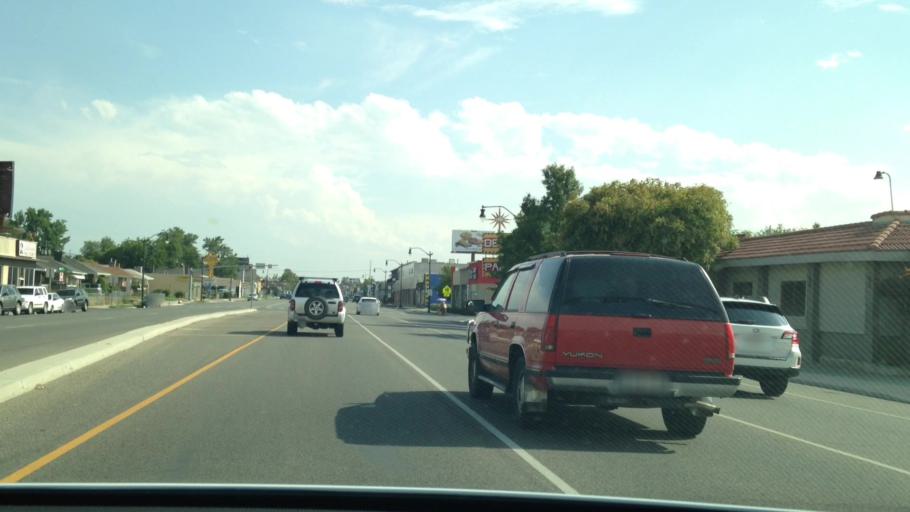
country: US
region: Utah
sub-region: Salt Lake County
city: Salt Lake City
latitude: 40.7457
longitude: -111.8883
